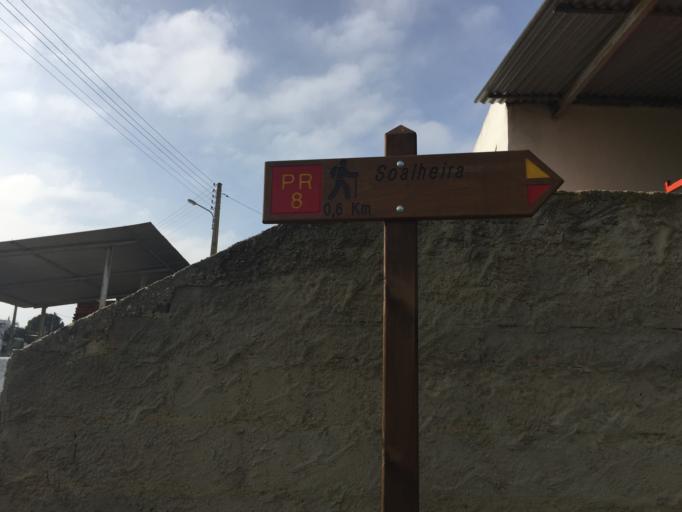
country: PT
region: Faro
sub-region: Castro Marim
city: Castro Marim
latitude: 37.3062
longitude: -7.5925
